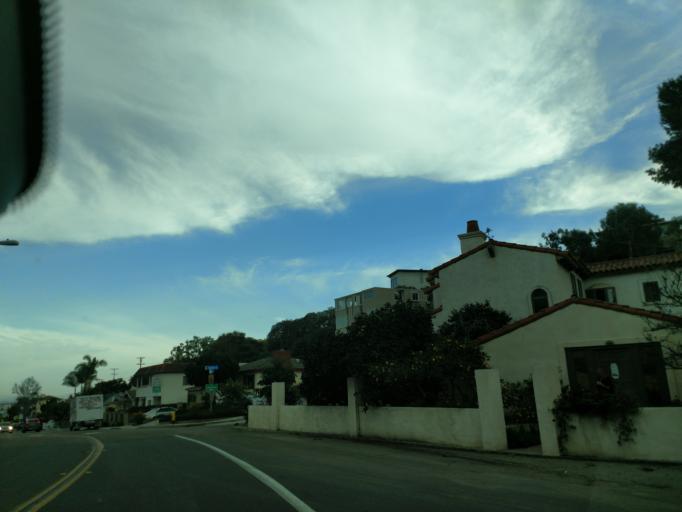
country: US
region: California
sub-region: San Diego County
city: Coronado
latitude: 32.7247
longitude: -117.2365
